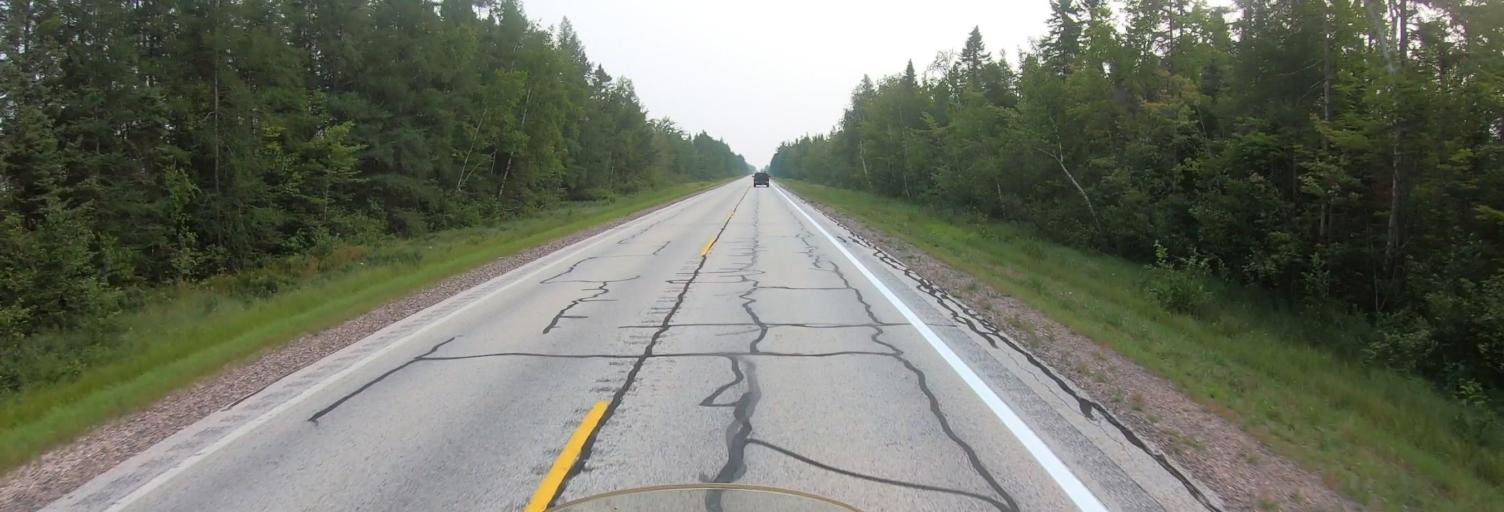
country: US
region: Michigan
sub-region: Luce County
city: Newberry
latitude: 46.5450
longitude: -85.0440
